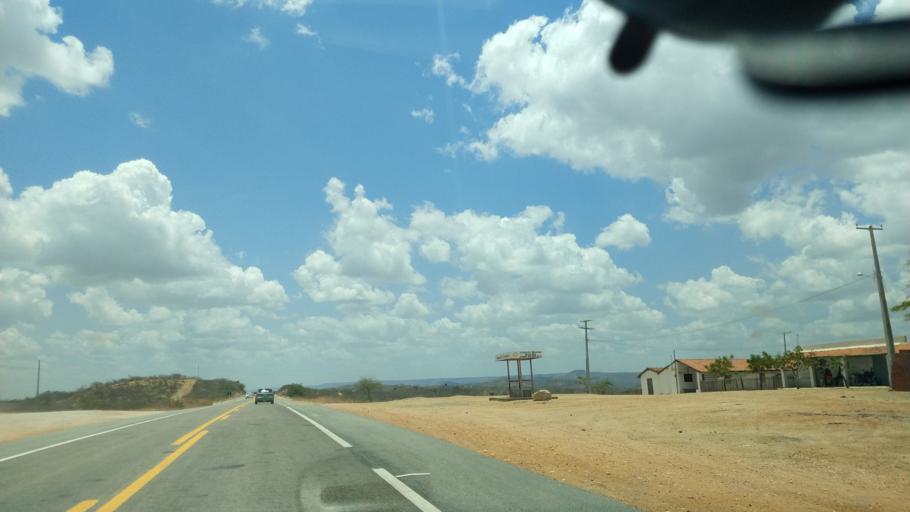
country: BR
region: Rio Grande do Norte
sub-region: Cerro Cora
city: Cerro Cora
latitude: -6.2065
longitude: -36.3194
